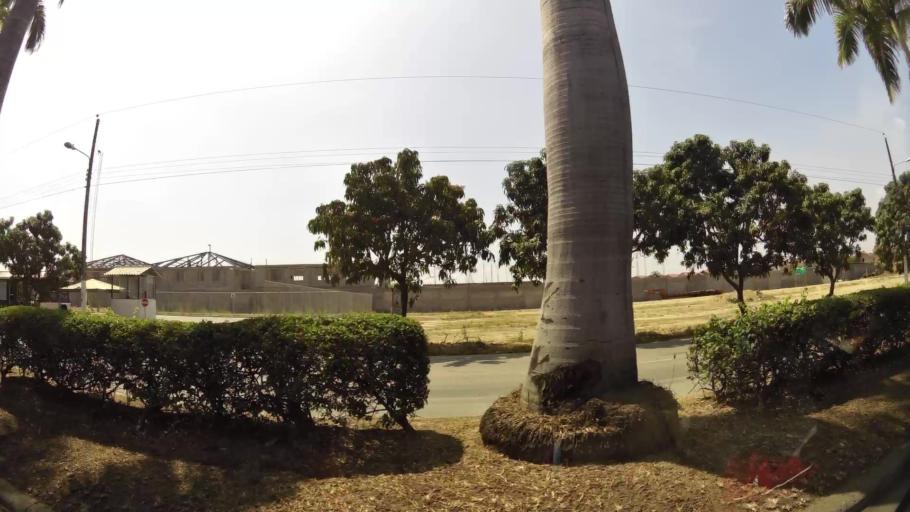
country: EC
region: Guayas
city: Eloy Alfaro
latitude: -2.0755
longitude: -79.8543
